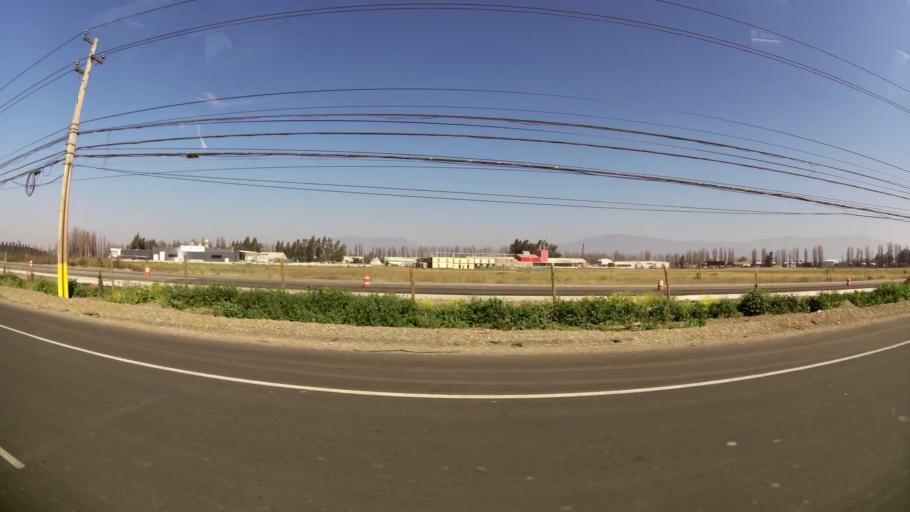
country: CL
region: Santiago Metropolitan
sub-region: Provincia de Chacabuco
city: Chicureo Abajo
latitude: -33.2882
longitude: -70.7355
